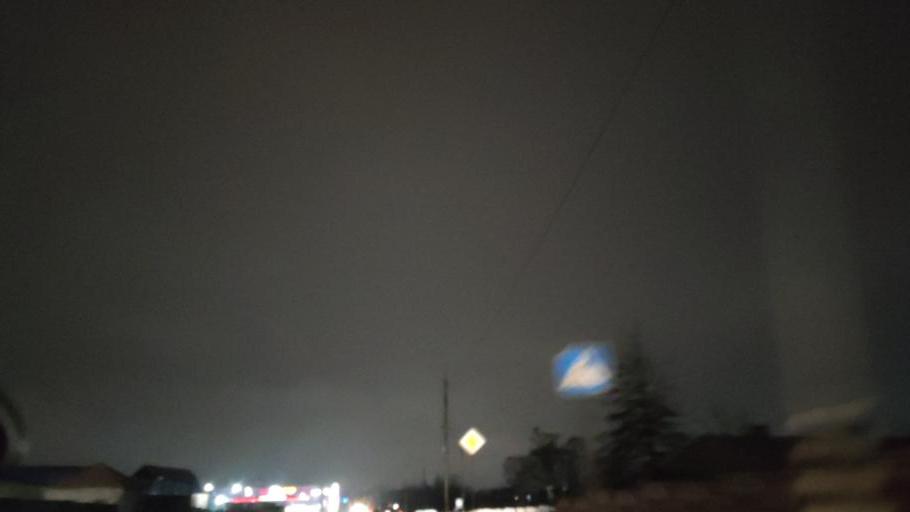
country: RU
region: Moskovskaya
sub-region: Podol'skiy Rayon
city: Podol'sk
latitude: 55.4359
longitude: 37.5982
